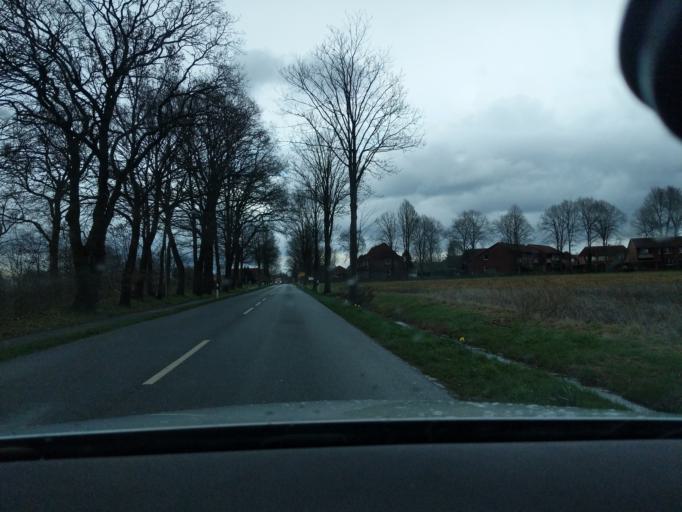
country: DE
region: Lower Saxony
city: Deinste
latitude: 53.5204
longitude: 9.3922
